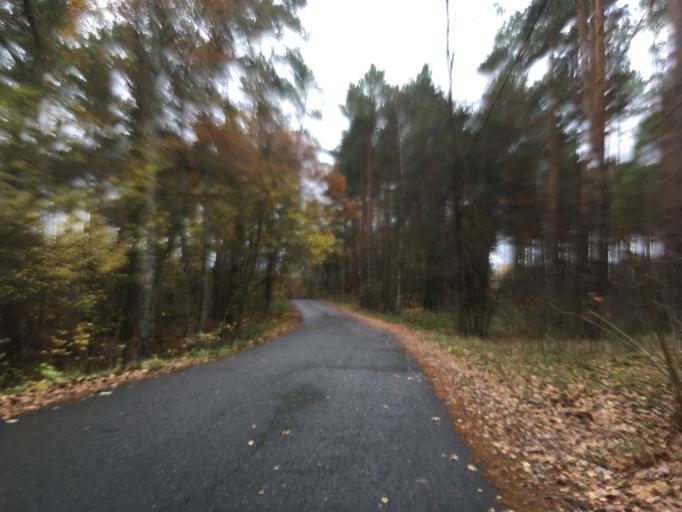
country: DE
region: Brandenburg
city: Mixdorf
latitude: 52.0959
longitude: 14.4338
